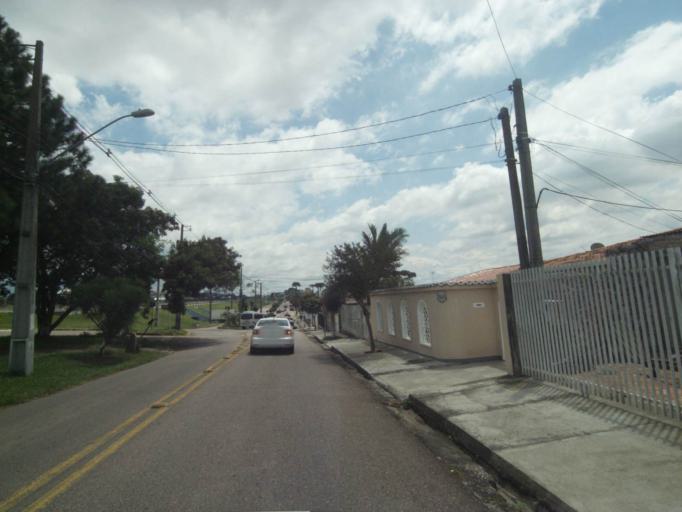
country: BR
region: Parana
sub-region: Pinhais
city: Pinhais
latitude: -25.4737
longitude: -49.2090
